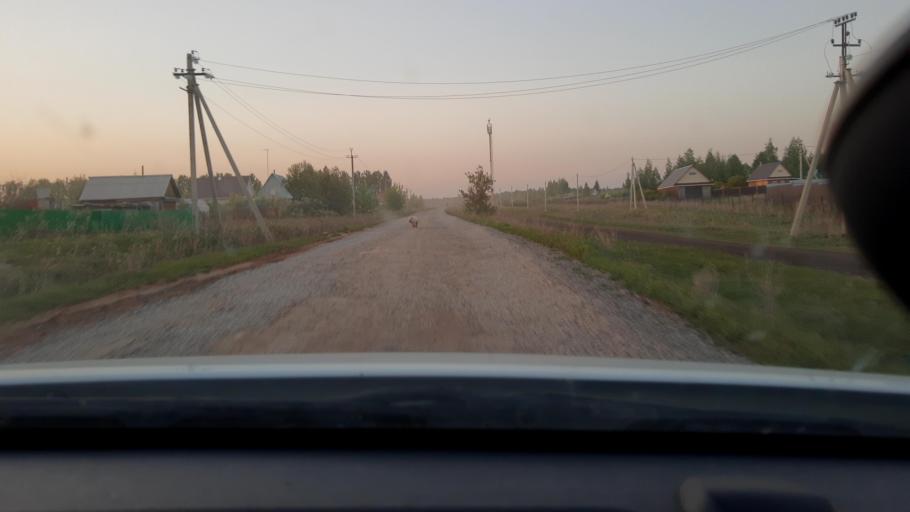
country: RU
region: Bashkortostan
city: Avdon
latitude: 54.5158
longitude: 55.8231
